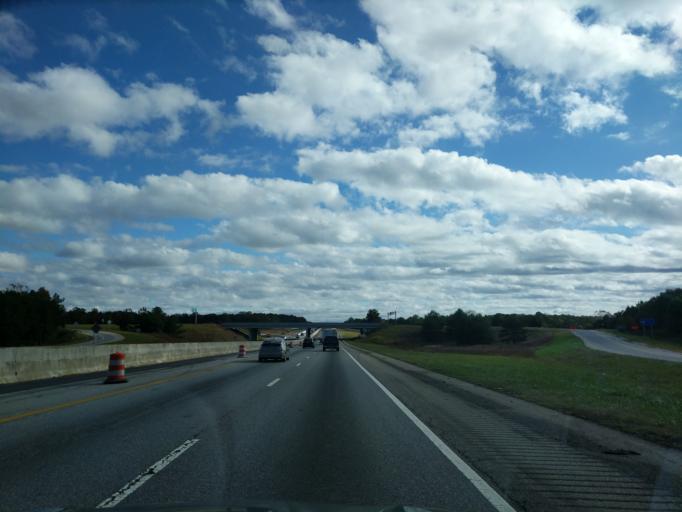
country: US
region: South Carolina
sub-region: Spartanburg County
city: Mayo
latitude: 35.0255
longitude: -81.8803
